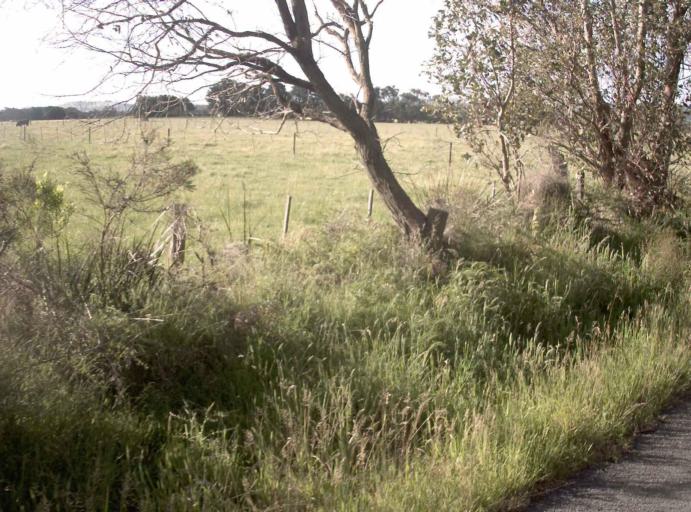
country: AU
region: Victoria
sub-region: Bass Coast
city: North Wonthaggi
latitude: -38.5568
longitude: 145.8435
